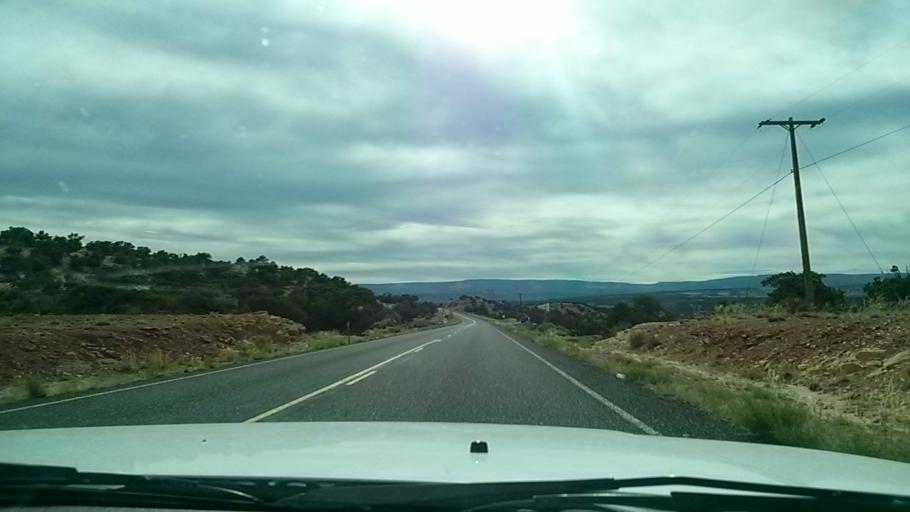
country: US
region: Utah
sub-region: Wayne County
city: Loa
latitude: 37.7507
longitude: -111.4614
